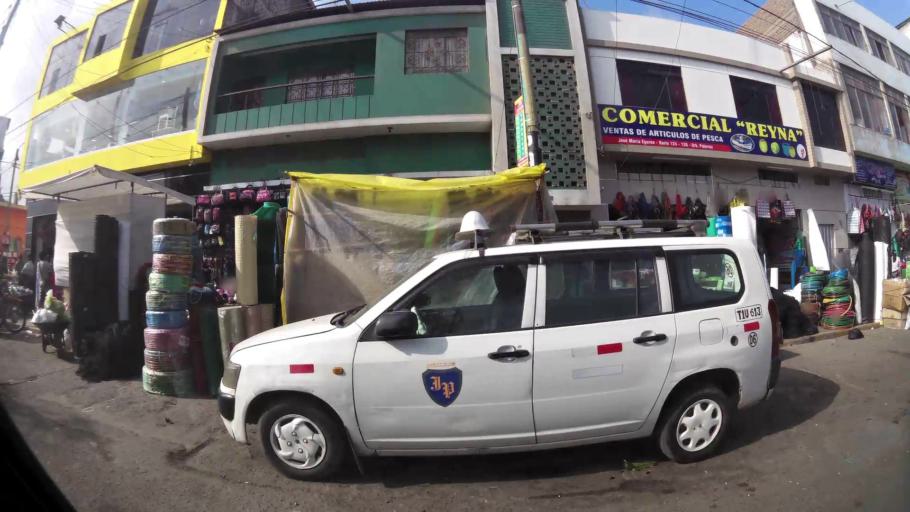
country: PE
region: La Libertad
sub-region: Provincia de Trujillo
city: Trujillo
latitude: -8.1113
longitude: -79.0193
